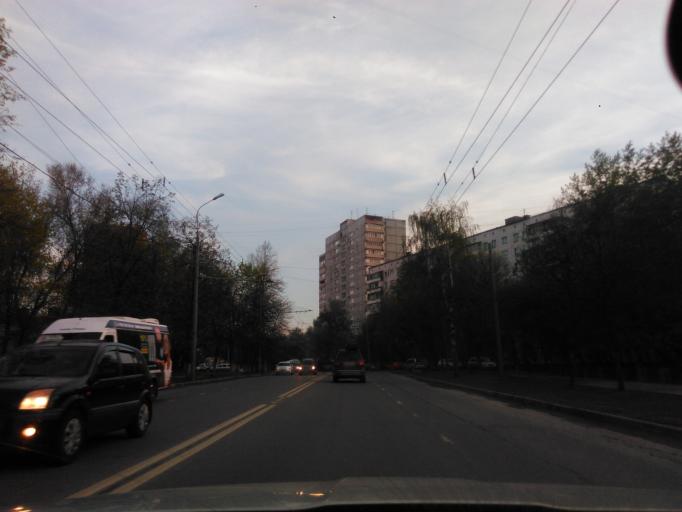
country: RU
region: Moscow
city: Lyublino
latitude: 55.6834
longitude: 37.7500
